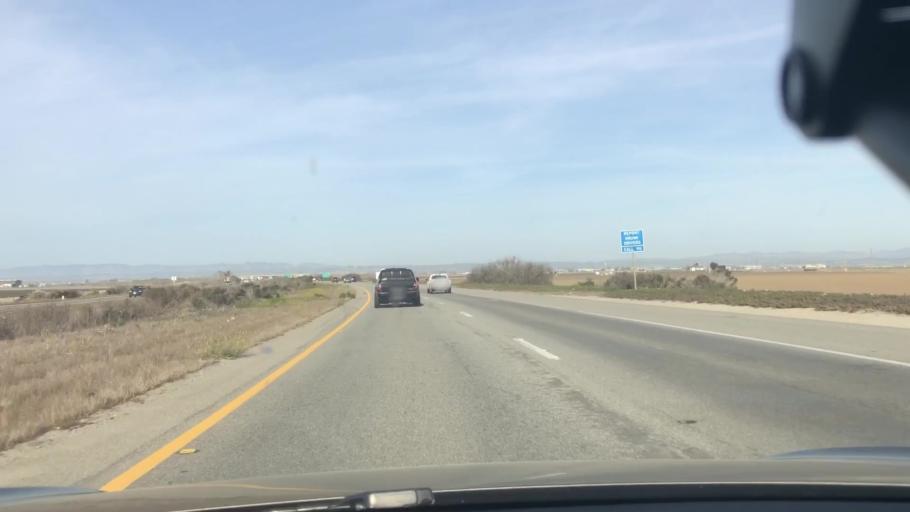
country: US
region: California
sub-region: Monterey County
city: Castroville
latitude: 36.7352
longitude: -121.7791
